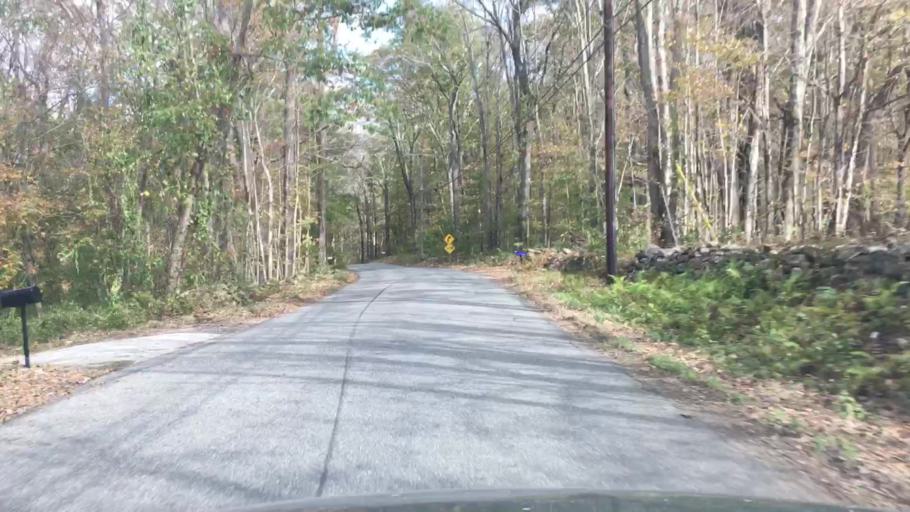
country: US
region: Connecticut
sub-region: Tolland County
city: Storrs
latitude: 41.8772
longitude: -72.1658
